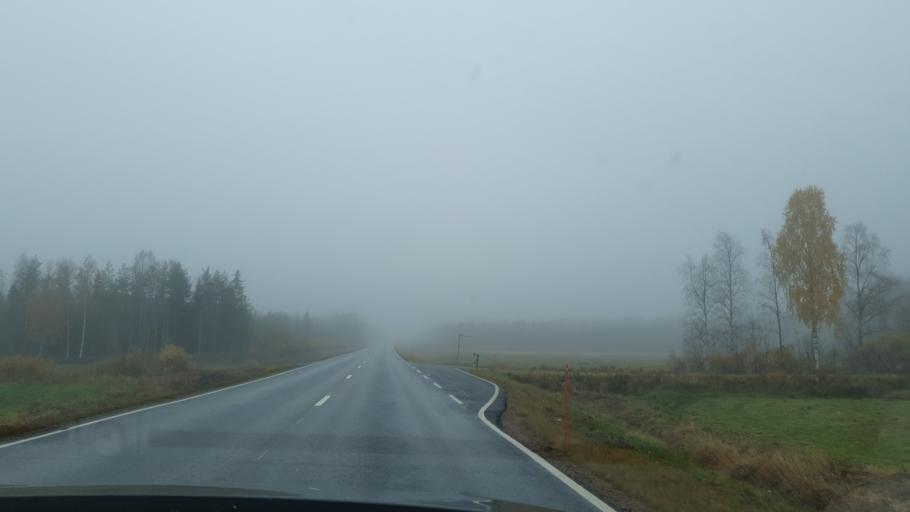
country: FI
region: Lapland
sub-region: Rovaniemi
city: Rovaniemi
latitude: 66.7993
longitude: 25.4142
